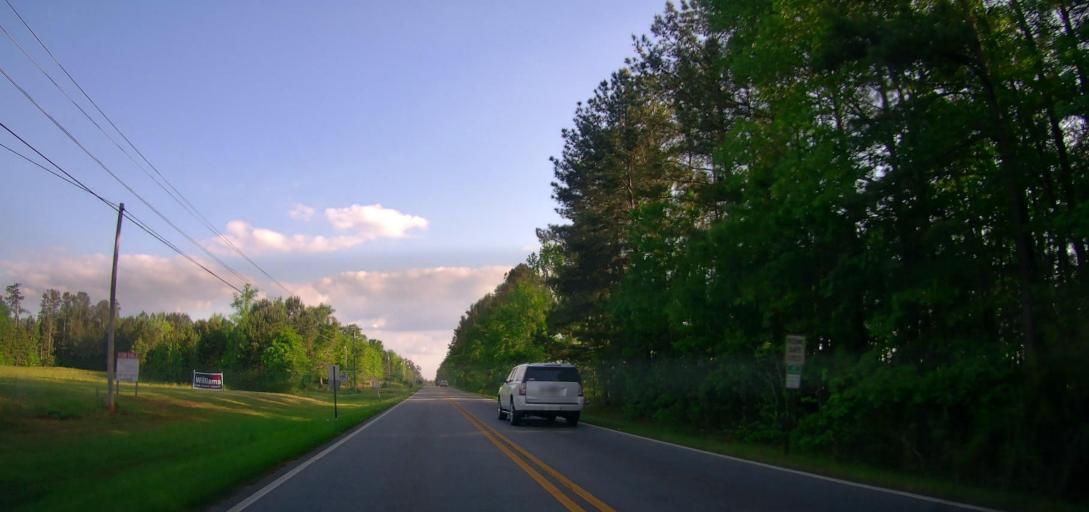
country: US
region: Georgia
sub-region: Putnam County
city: Eatonton
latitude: 33.2698
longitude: -83.3015
